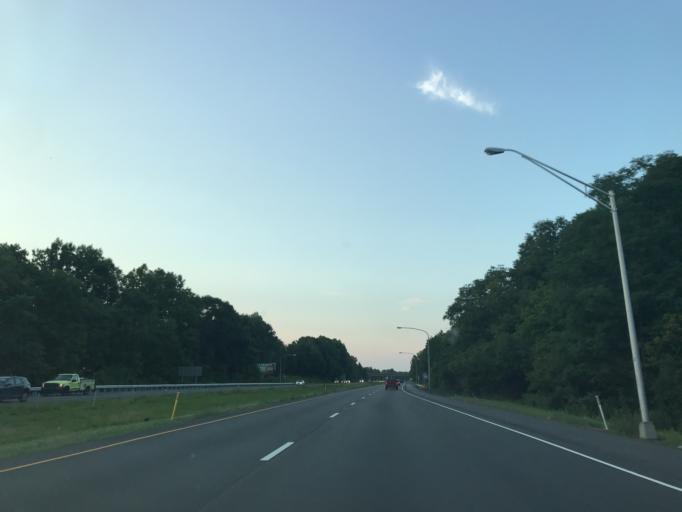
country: US
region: Pennsylvania
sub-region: Bucks County
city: Langhorne Manor
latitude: 40.1706
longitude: -74.8987
